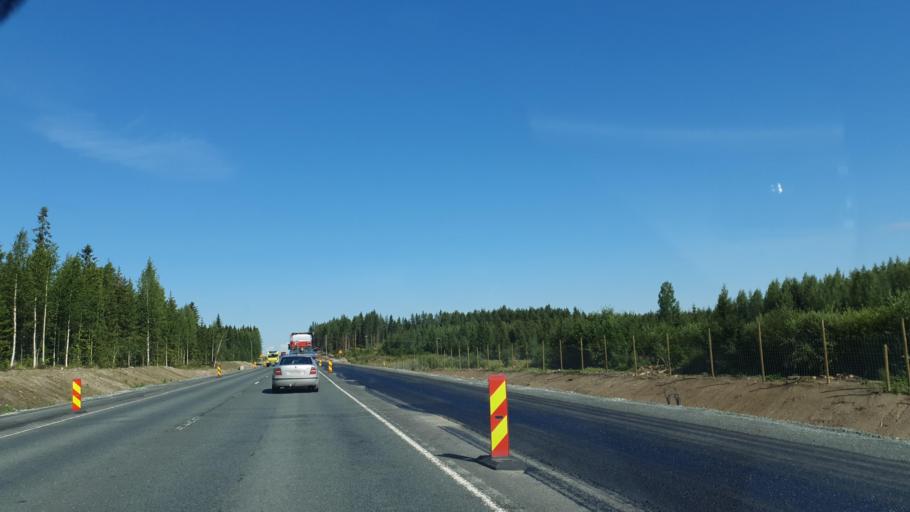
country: FI
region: Northern Savo
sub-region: Ylae-Savo
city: Lapinlahti
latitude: 63.3000
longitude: 27.4519
